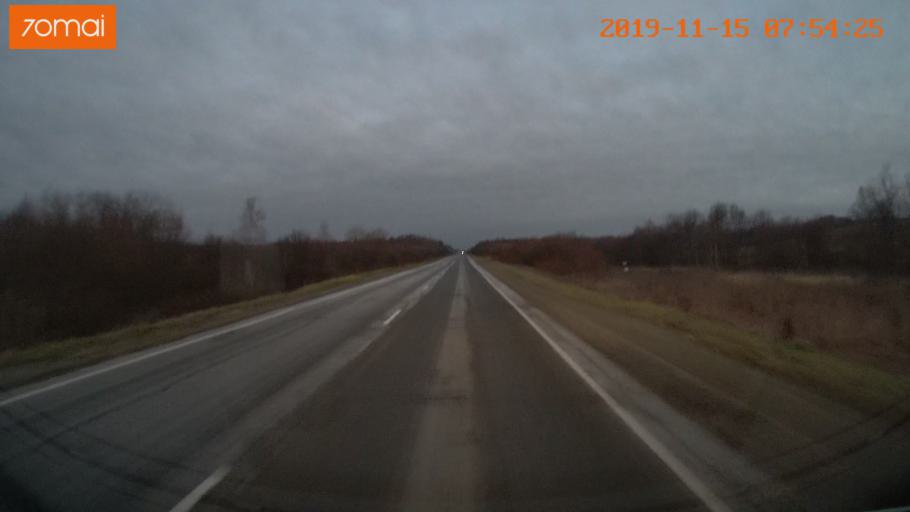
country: RU
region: Vologda
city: Cherepovets
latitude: 58.8977
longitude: 38.1770
